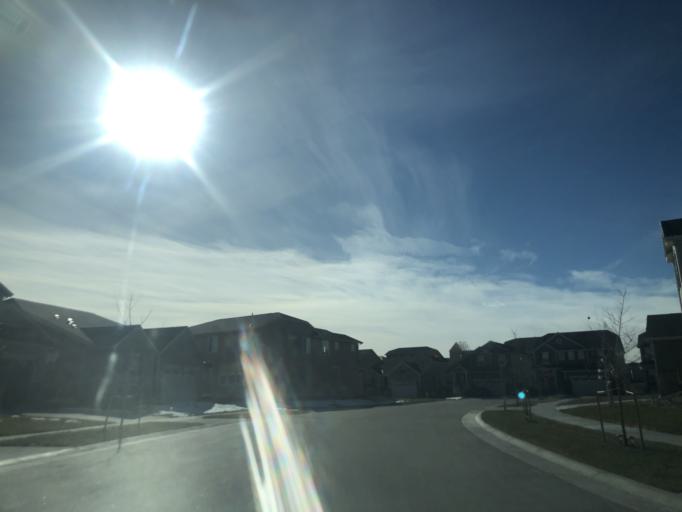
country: US
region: Colorado
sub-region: Douglas County
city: Stonegate
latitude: 39.5569
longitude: -104.8019
